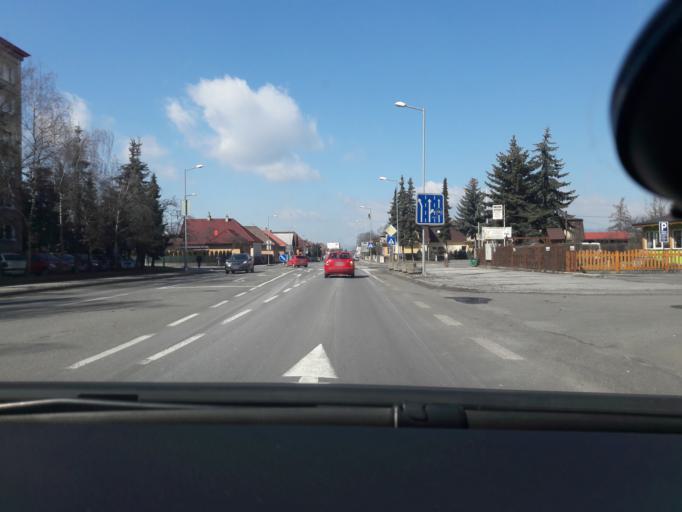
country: SK
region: Zilinsky
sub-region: Okres Liptovsky Mikulas
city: Liptovsky Mikulas
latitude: 49.0795
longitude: 19.6290
